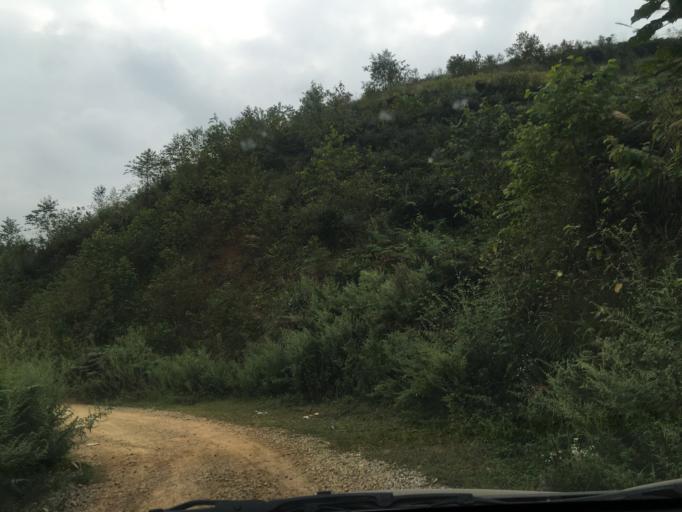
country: CN
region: Guangxi Zhuangzu Zizhiqu
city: Xinzhou
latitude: 25.5424
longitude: 105.5334
